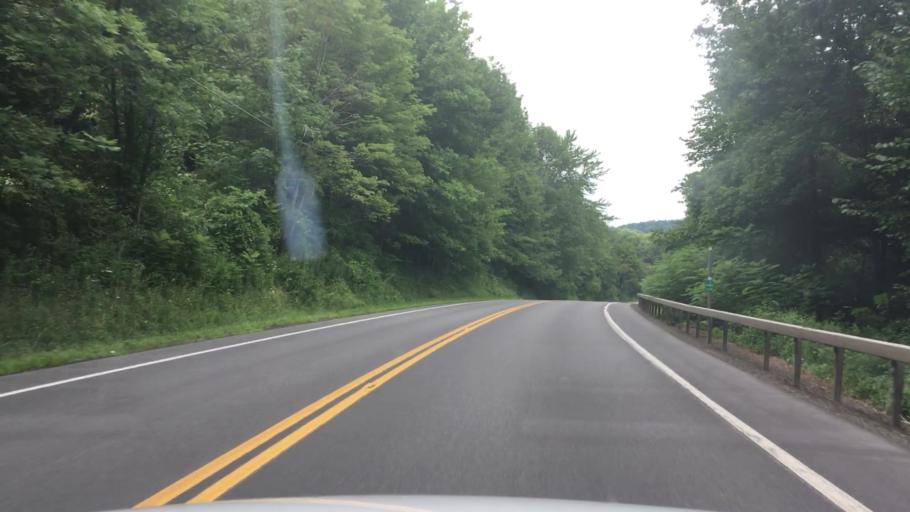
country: US
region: New York
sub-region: Otsego County
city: Otego
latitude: 42.4104
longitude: -75.1499
